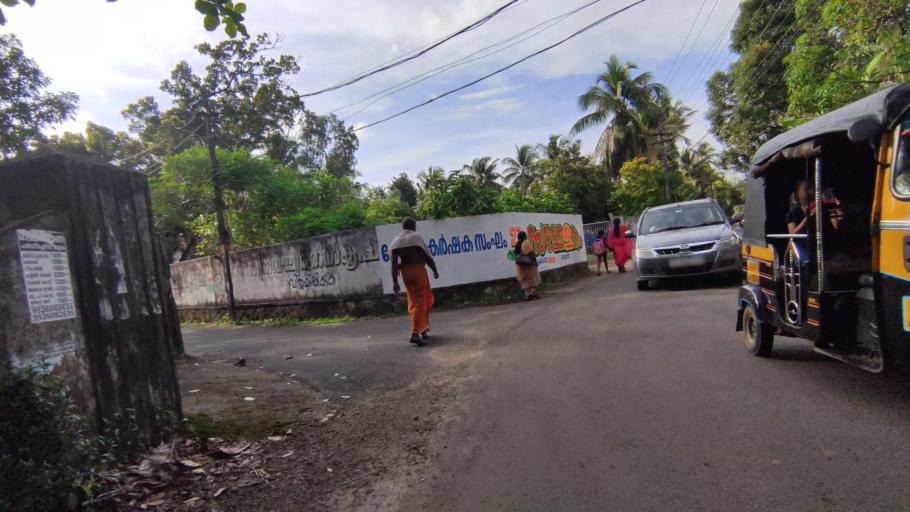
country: IN
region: Kerala
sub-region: Kottayam
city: Kottayam
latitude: 9.5839
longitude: 76.4989
